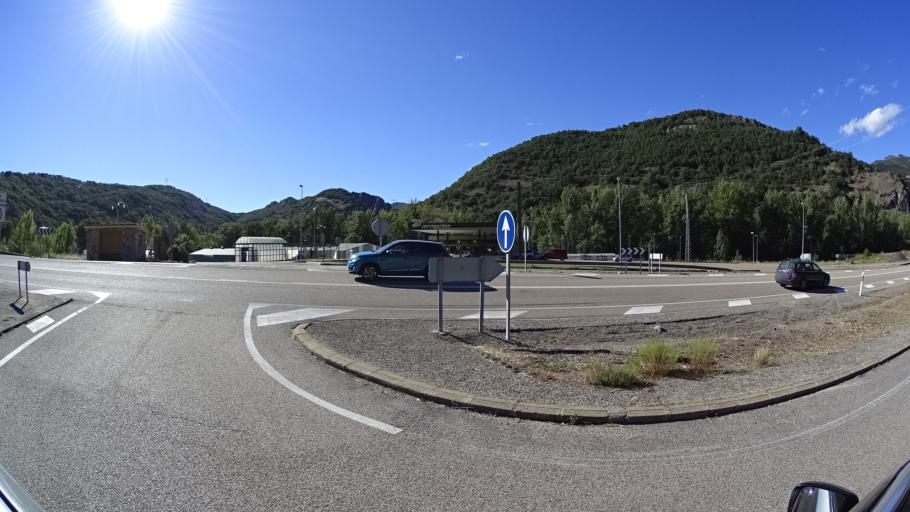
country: ES
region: Castille and Leon
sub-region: Provincia de Leon
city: La Pola de Gordon
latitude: 42.8617
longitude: -5.6731
